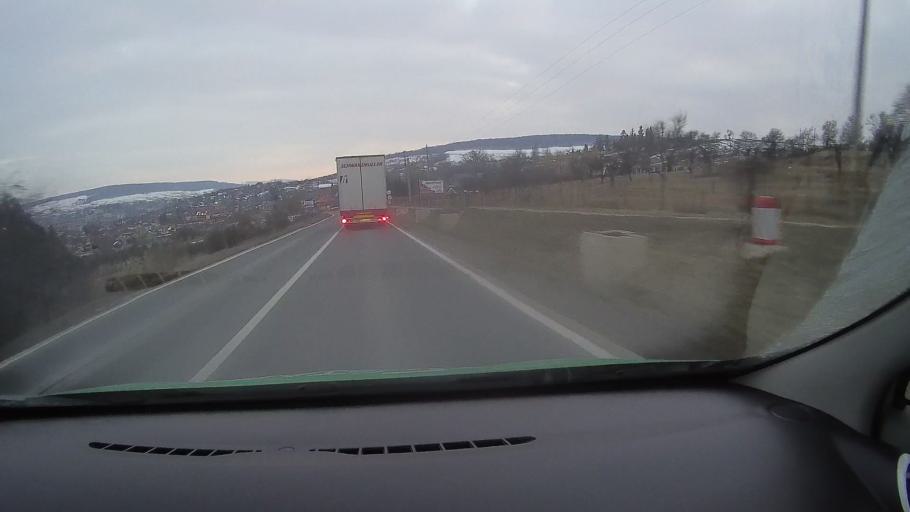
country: RO
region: Harghita
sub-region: Municipiul Odorheiu Secuiesc
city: Odorheiu Secuiesc
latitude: 46.3213
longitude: 25.2801
